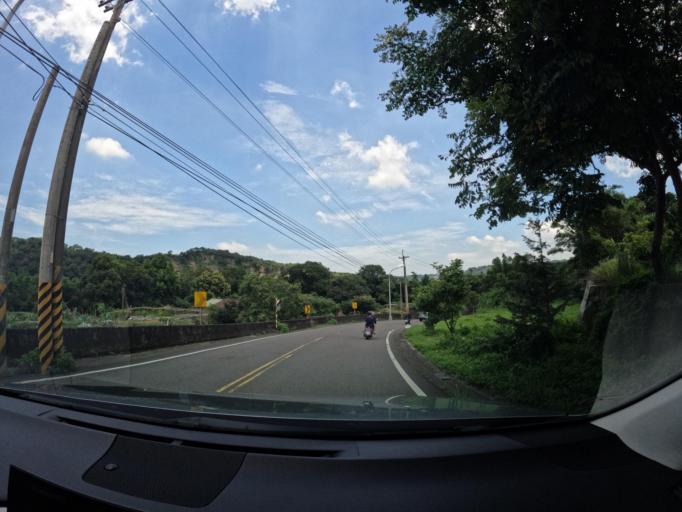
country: TW
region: Taiwan
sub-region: Hsinchu
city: Hsinchu
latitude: 24.6579
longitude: 120.9579
